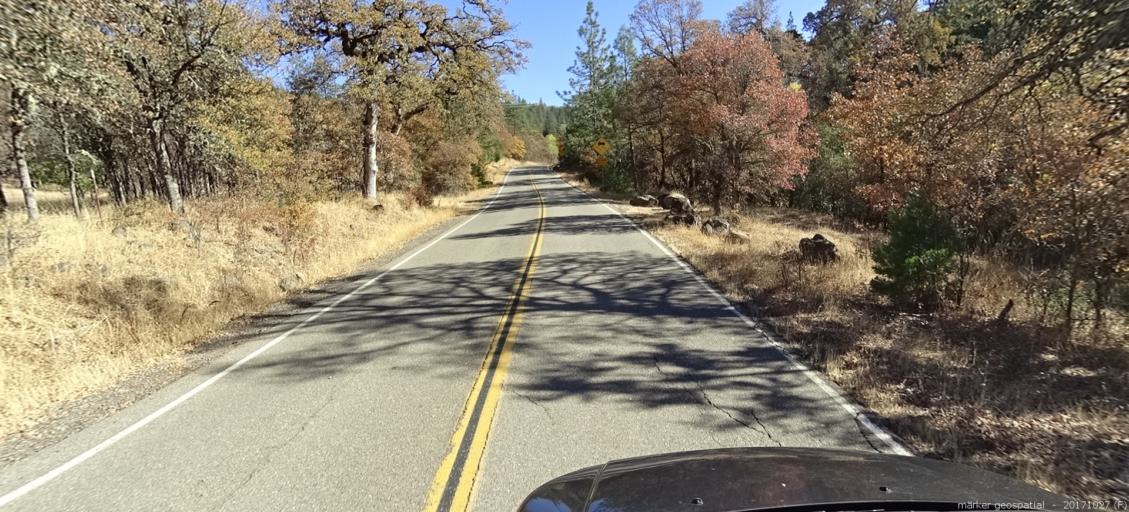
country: US
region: California
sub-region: Shasta County
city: Shingletown
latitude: 40.7035
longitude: -121.9218
